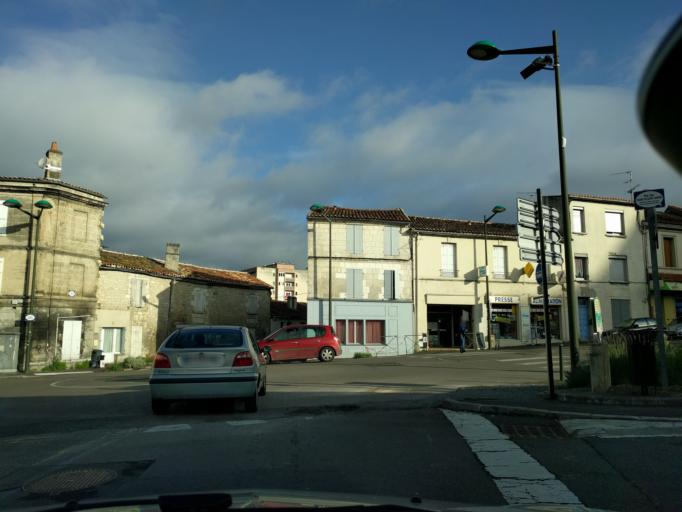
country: FR
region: Poitou-Charentes
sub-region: Departement de la Charente
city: Angouleme
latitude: 45.6497
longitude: 0.1444
